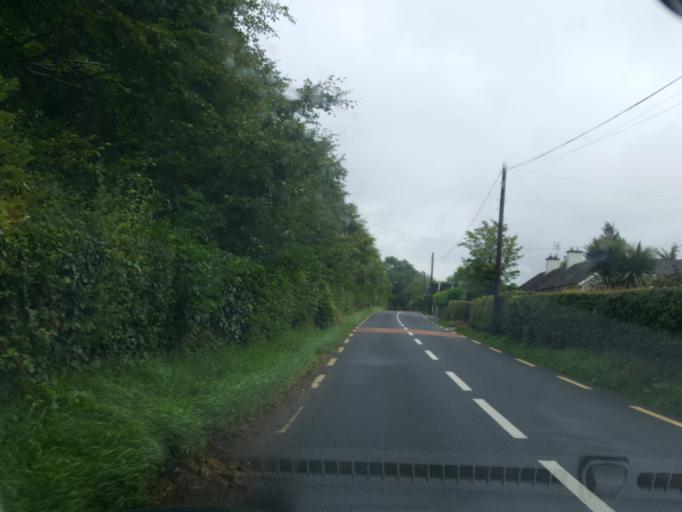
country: IE
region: Leinster
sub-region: Kildare
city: Kilcullen
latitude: 53.1197
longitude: -6.7287
